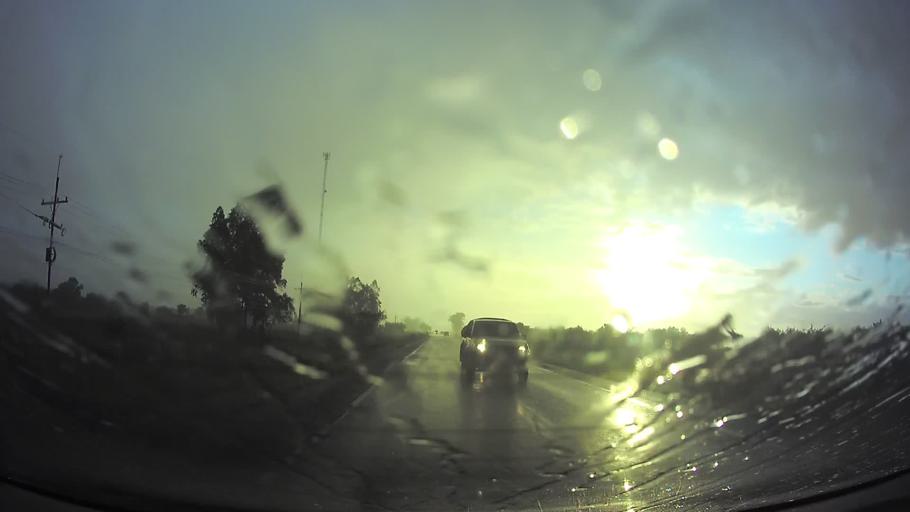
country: PY
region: Paraguari
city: Paraguari
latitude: -25.6949
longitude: -57.1718
